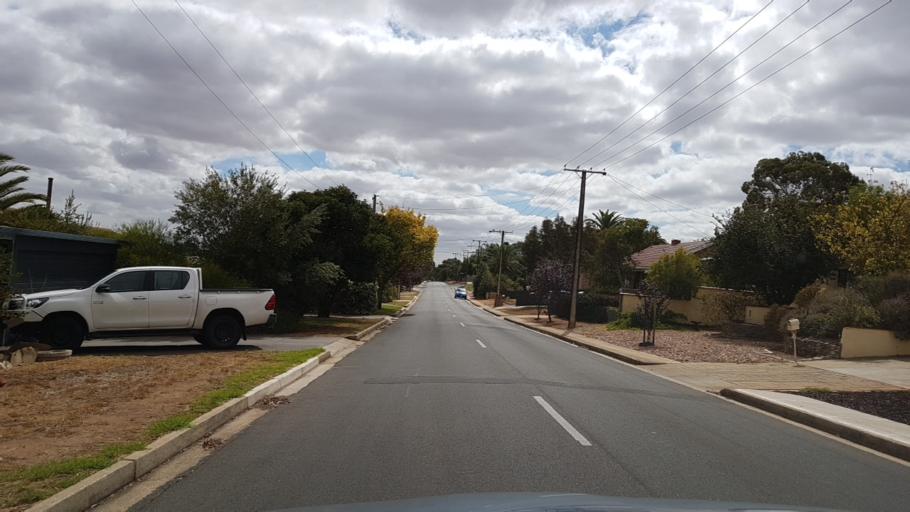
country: AU
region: South Australia
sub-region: Gawler
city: Gawler
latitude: -34.6086
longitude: 138.7534
